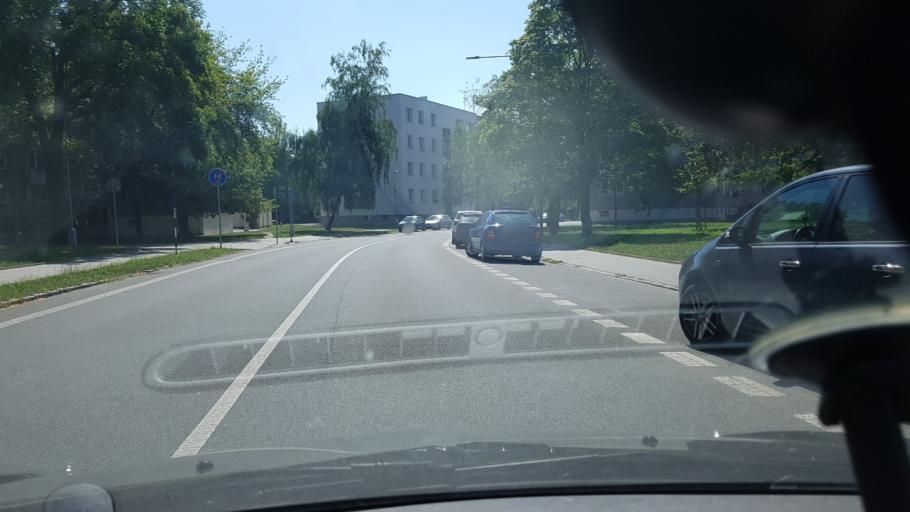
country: CZ
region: Moravskoslezsky
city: Bohumin
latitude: 49.9047
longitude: 18.3511
